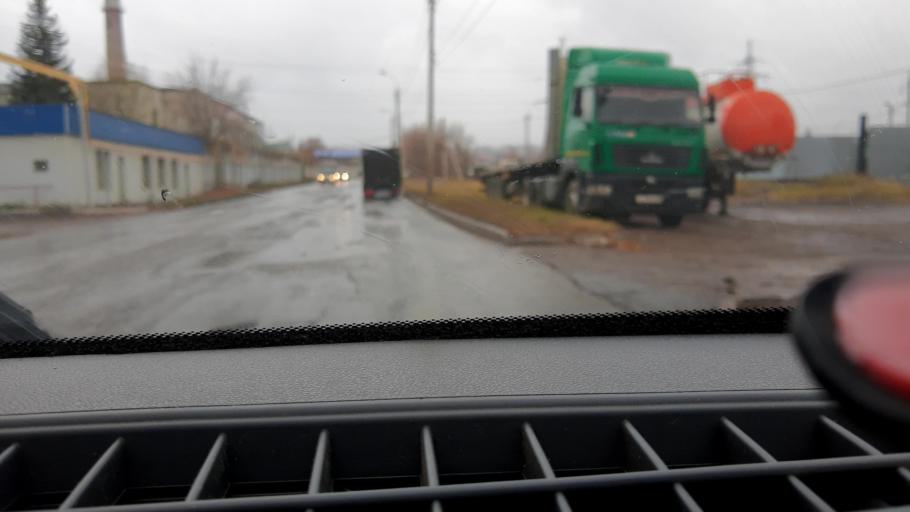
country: RU
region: Bashkortostan
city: Avdon
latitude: 54.6856
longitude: 55.8124
